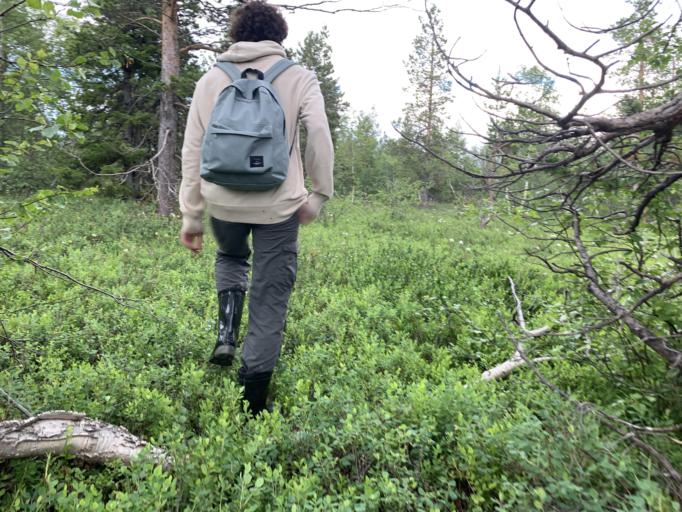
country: RU
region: Murmansk
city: Olenegorsk
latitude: 67.8580
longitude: 33.2035
